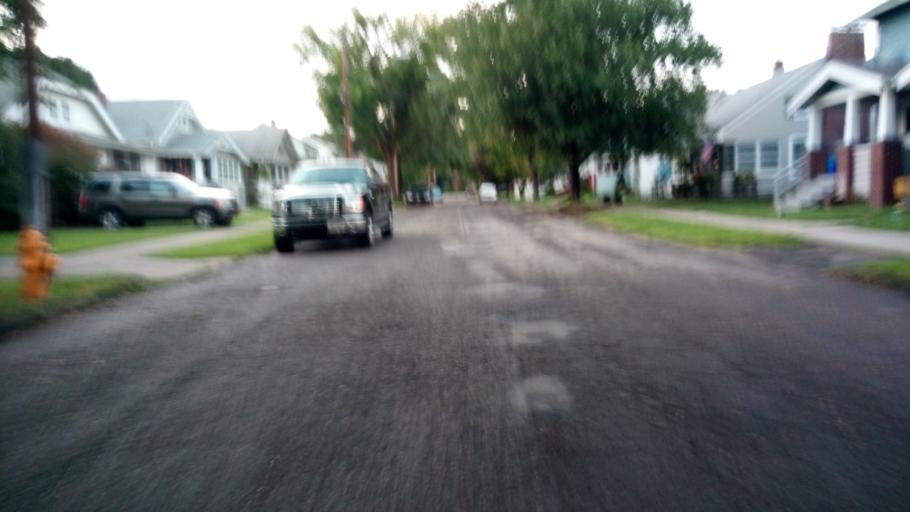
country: US
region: New York
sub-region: Chemung County
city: Elmira
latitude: 42.0971
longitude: -76.8267
